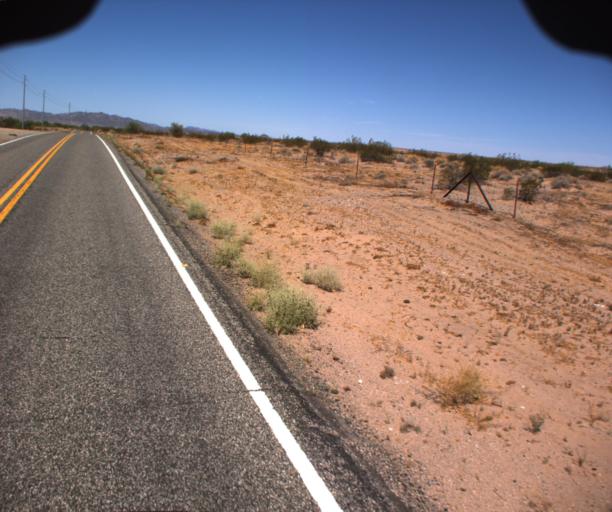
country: US
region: Arizona
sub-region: La Paz County
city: Cienega Springs
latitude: 33.9933
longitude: -114.1250
